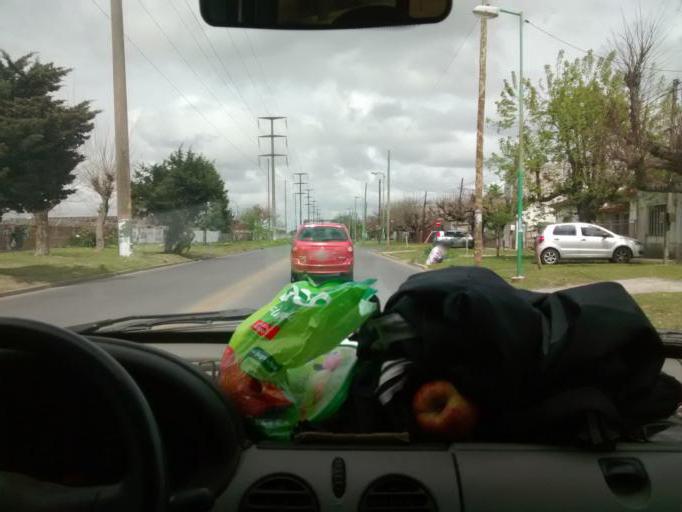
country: AR
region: Buenos Aires
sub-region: Partido de La Plata
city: La Plata
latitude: -34.9402
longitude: -57.9753
